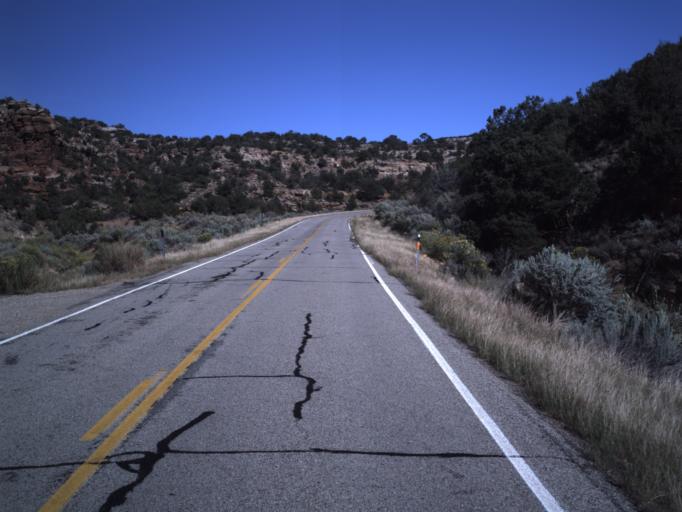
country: US
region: Utah
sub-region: San Juan County
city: Monticello
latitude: 37.9858
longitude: -109.5128
